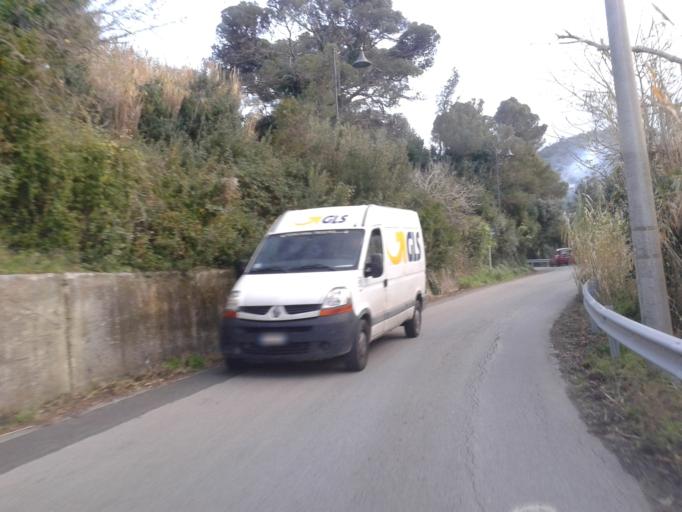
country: IT
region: Tuscany
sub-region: Provincia di Livorno
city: Quercianella
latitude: 43.4971
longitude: 10.3552
